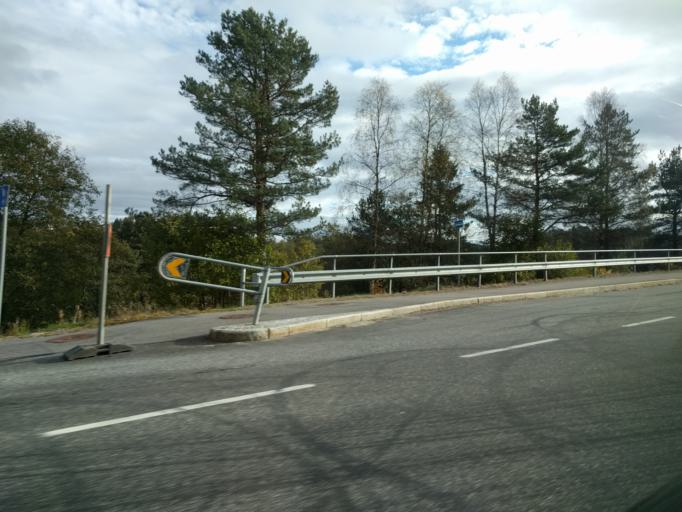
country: NO
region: Vest-Agder
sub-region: Vennesla
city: Vennesla
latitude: 58.2943
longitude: 7.8406
